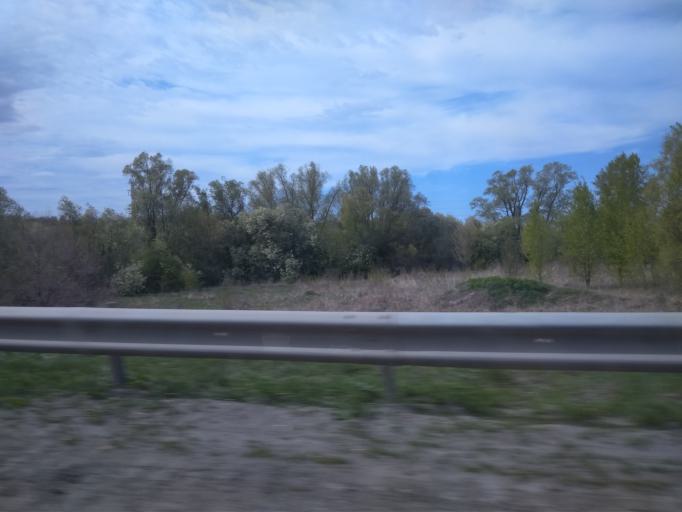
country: RU
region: Mordoviya
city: Atemar
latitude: 54.3196
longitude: 45.4806
